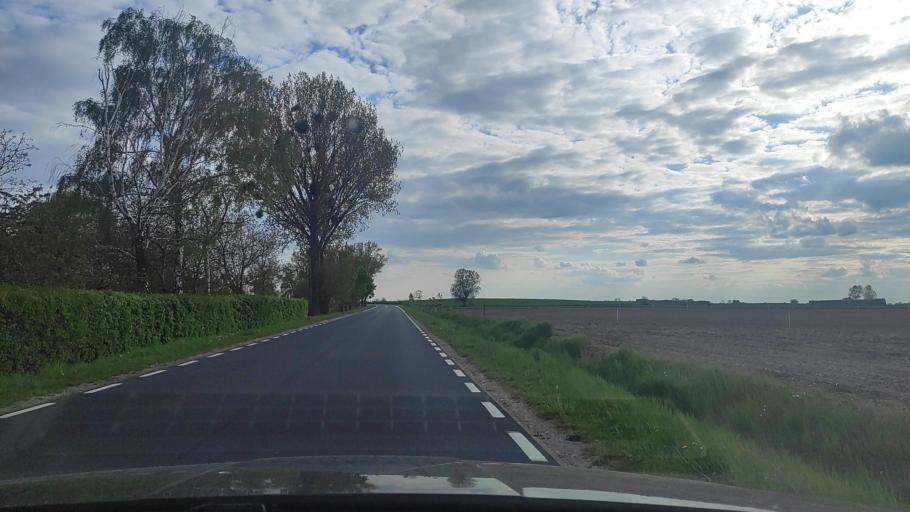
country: PL
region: Greater Poland Voivodeship
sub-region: Powiat poznanski
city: Kostrzyn
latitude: 52.4343
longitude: 17.2352
